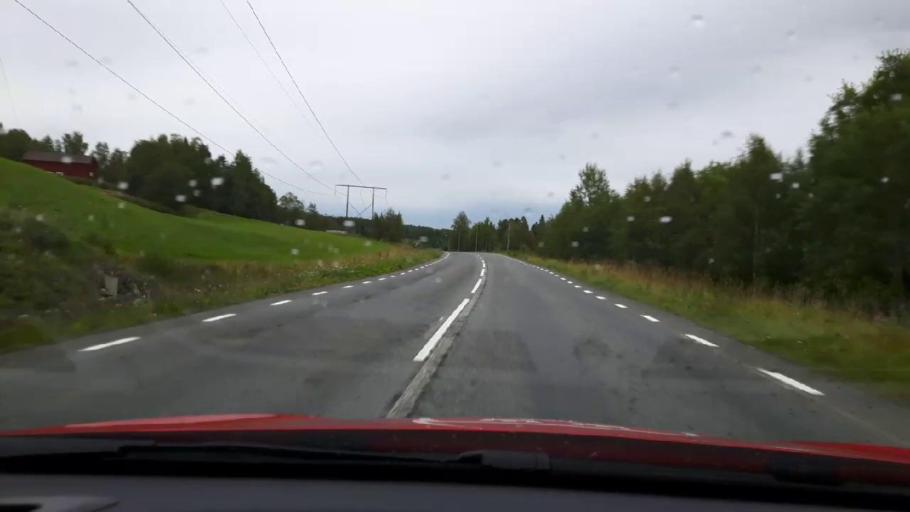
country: SE
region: Jaemtland
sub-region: Are Kommun
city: Jarpen
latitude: 63.3878
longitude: 13.4032
